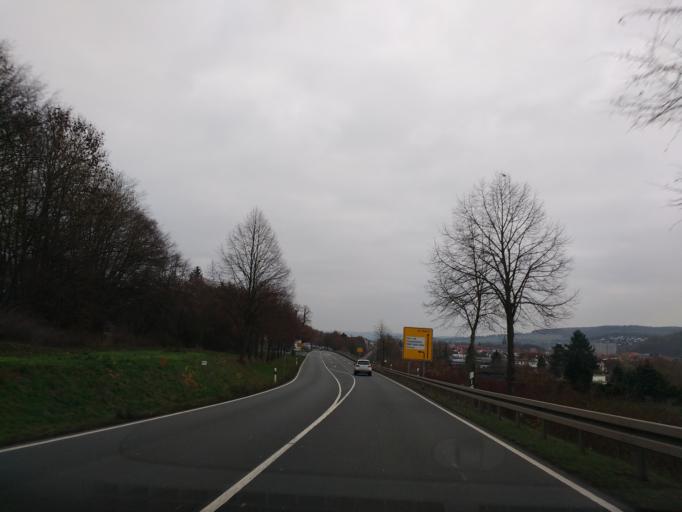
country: DE
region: Hesse
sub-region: Regierungsbezirk Kassel
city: Rotenburg an der Fulda
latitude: 51.0057
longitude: 9.7200
